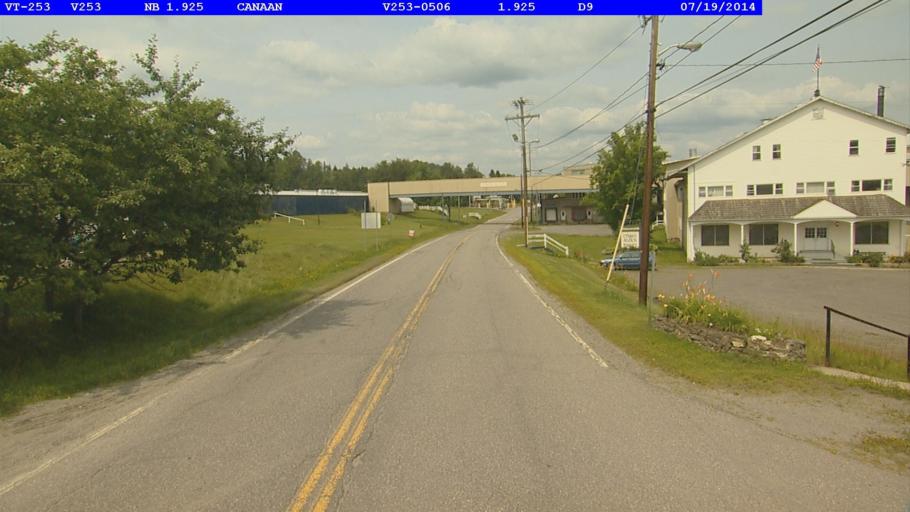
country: US
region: New Hampshire
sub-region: Coos County
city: Colebrook
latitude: 45.0102
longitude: -71.5068
